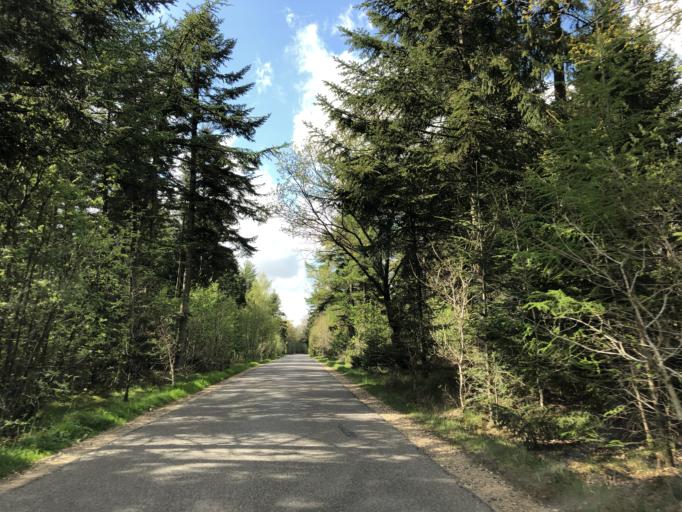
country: DK
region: Central Jutland
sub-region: Herning Kommune
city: Avlum
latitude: 56.2992
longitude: 8.6996
